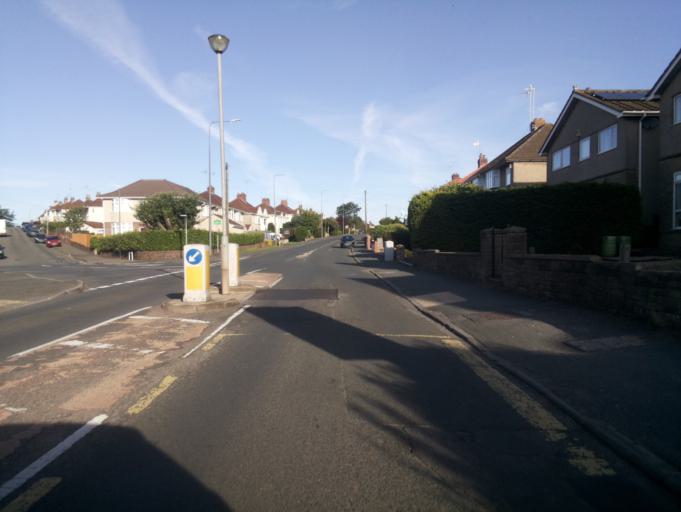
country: GB
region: England
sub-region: South Gloucestershire
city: Mangotsfield
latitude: 51.4882
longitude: -2.4951
